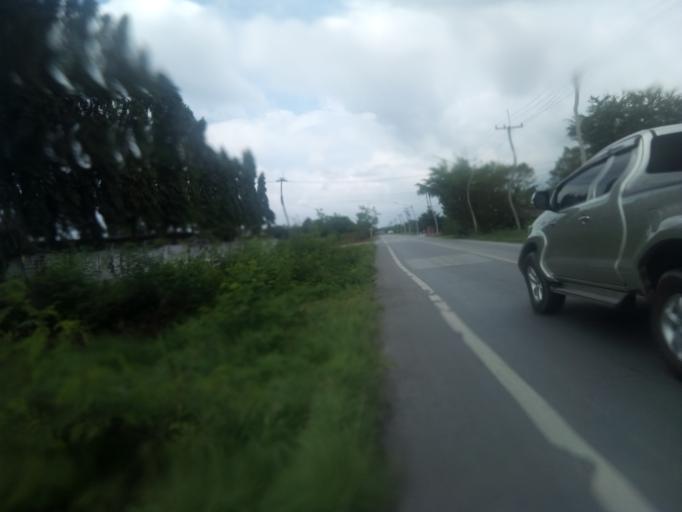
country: TH
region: Pathum Thani
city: Ban Lam Luk Ka
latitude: 13.9892
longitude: 100.8211
